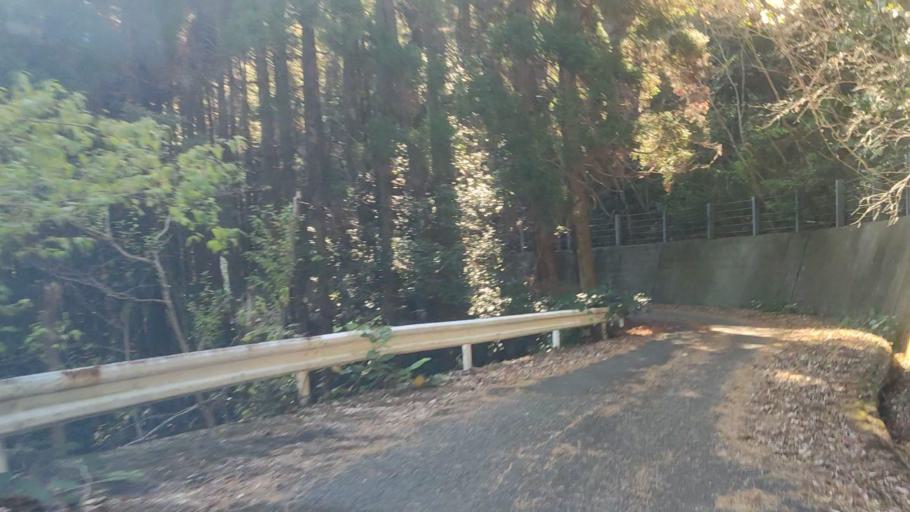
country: JP
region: Oita
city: Saiki
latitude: 32.7845
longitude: 131.8583
